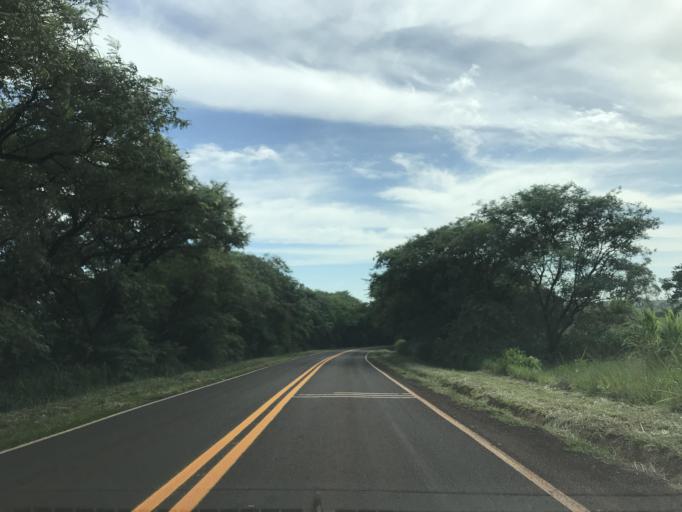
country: BR
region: Parana
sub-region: Terra Rica
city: Terra Rica
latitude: -22.7779
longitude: -52.6561
